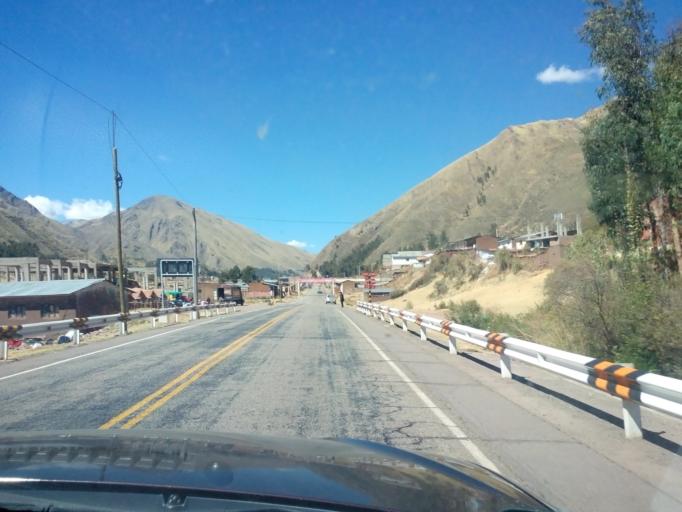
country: PE
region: Cusco
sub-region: Provincia de Canchis
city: Marangani
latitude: -14.3544
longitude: -71.1691
